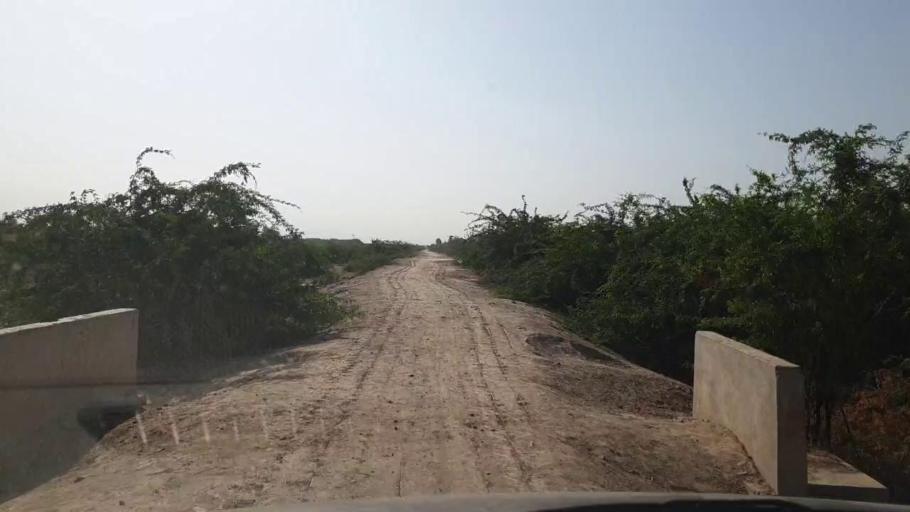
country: PK
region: Sindh
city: Kadhan
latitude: 24.5758
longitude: 69.0811
